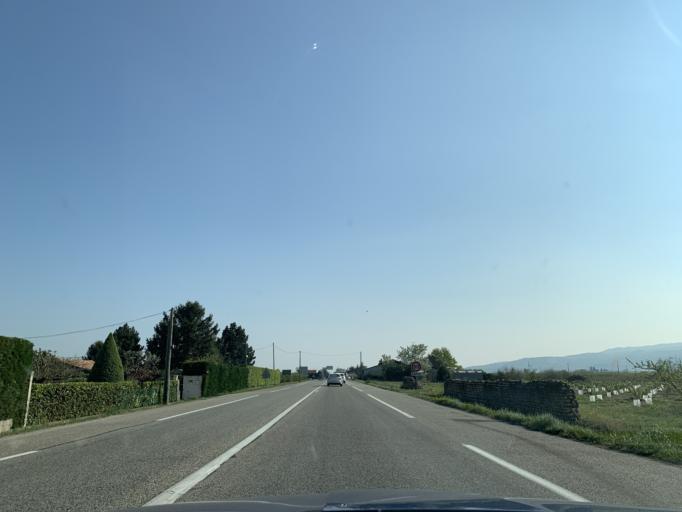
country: FR
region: Rhone-Alpes
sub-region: Departement de la Drome
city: Mercurol
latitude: 45.0483
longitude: 4.8667
